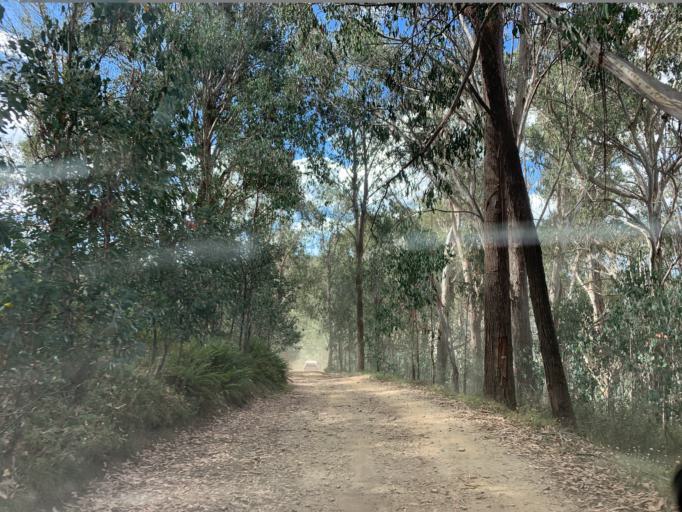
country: AU
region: Victoria
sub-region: Mansfield
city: Mansfield
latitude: -37.1086
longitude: 146.5345
